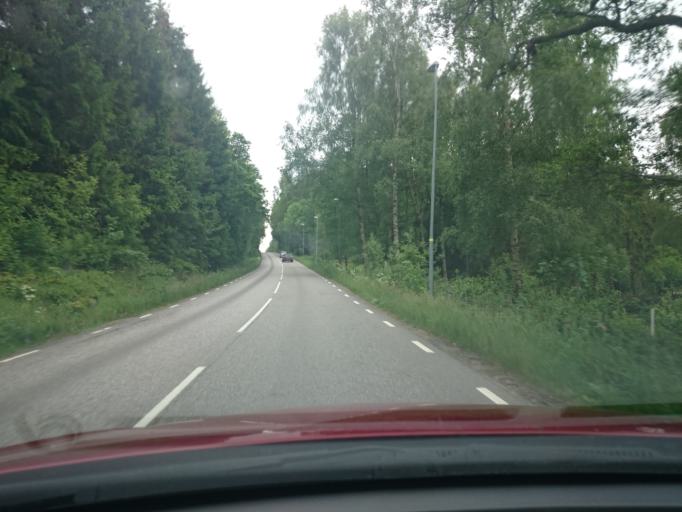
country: SE
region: Vaestra Goetaland
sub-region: Lerums Kommun
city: Lerum
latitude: 57.7717
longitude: 12.2984
